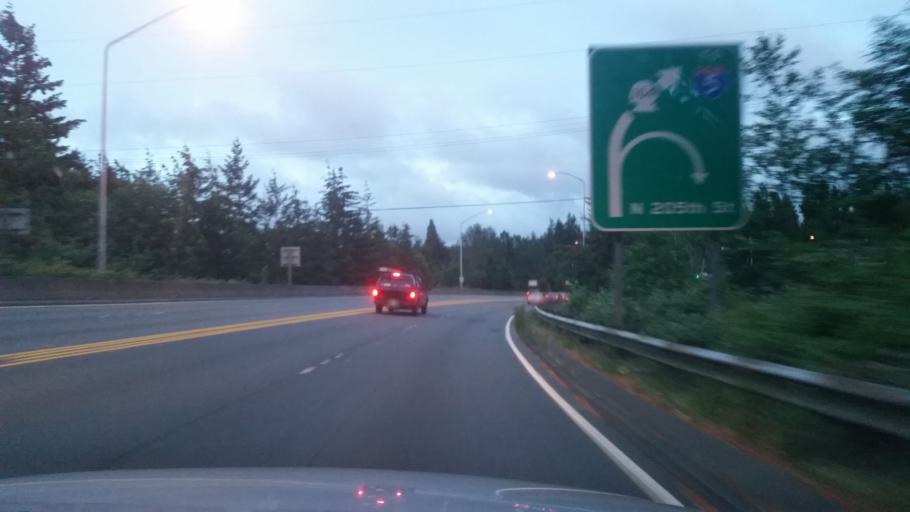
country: US
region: Washington
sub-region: Snohomish County
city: Esperance
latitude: 47.7788
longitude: -122.3417
